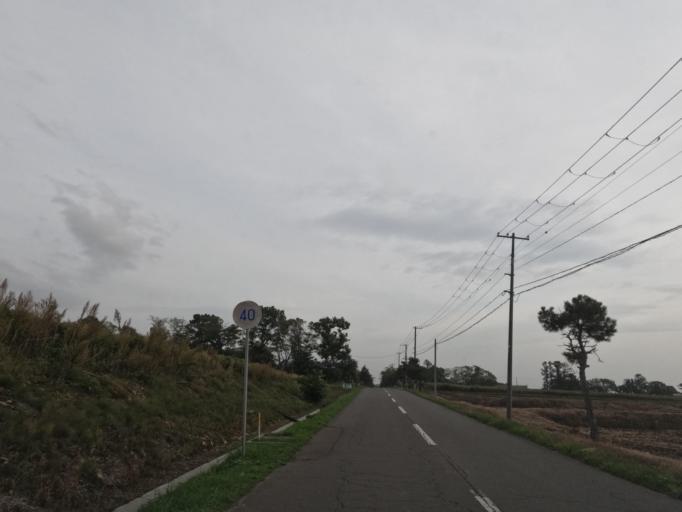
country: JP
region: Hokkaido
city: Date
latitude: 42.4347
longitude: 140.9084
